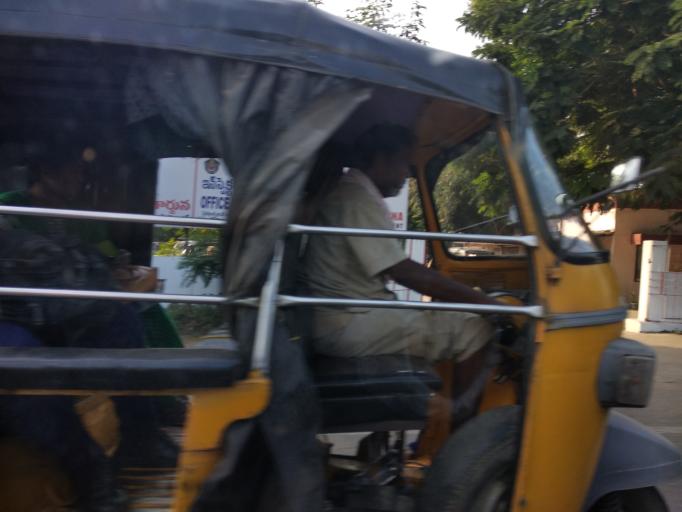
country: IN
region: Andhra Pradesh
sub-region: Vishakhapatnam
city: Visakhapatnam
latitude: 17.6850
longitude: 83.1662
